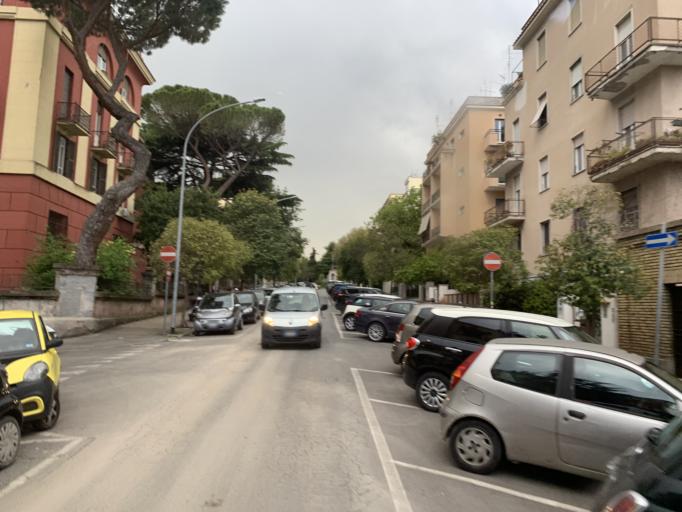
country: VA
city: Vatican City
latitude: 41.8852
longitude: 12.4577
